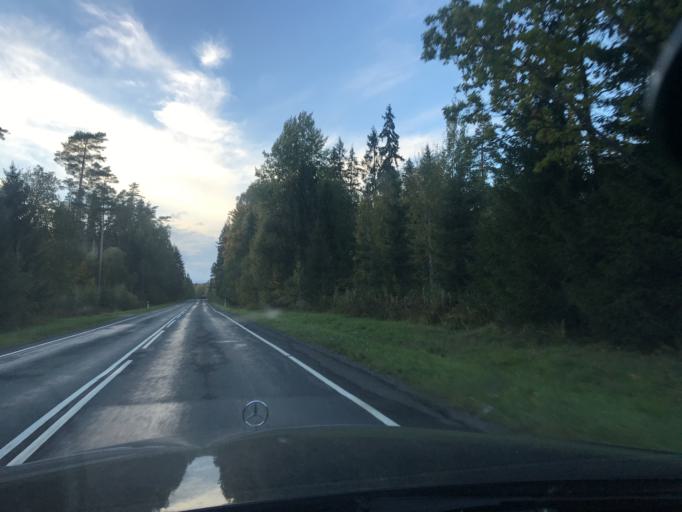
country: EE
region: Vorumaa
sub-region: Antsla vald
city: Vana-Antsla
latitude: 57.8754
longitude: 26.5871
